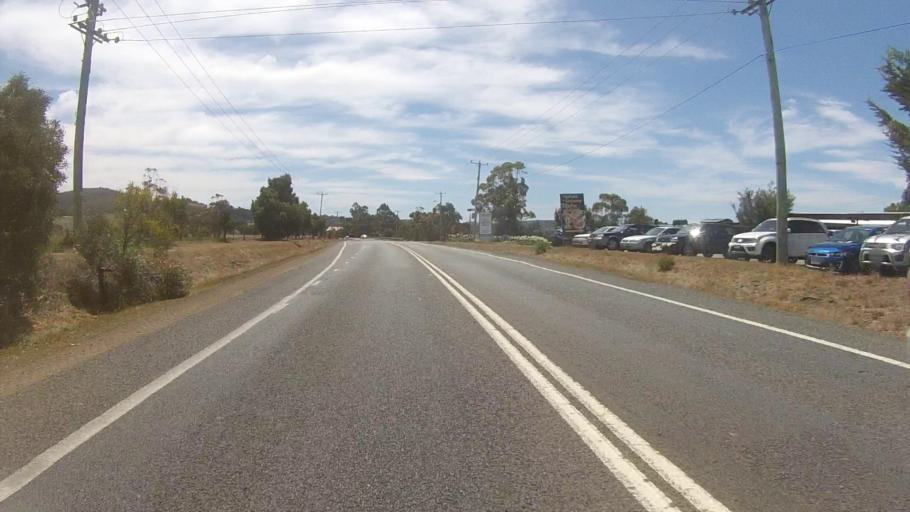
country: AU
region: Tasmania
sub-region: Kingborough
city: Margate
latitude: -43.0182
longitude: 147.2699
